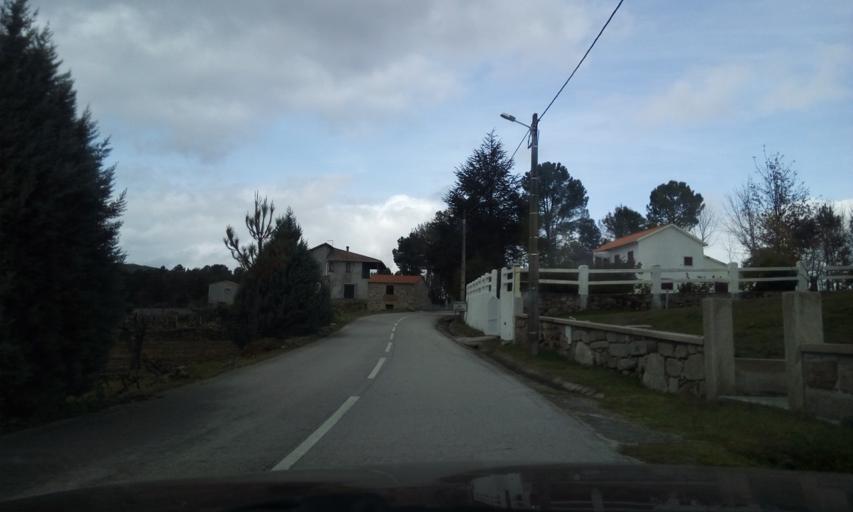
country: PT
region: Guarda
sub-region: Fornos de Algodres
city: Fornos de Algodres
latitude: 40.6612
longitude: -7.5982
